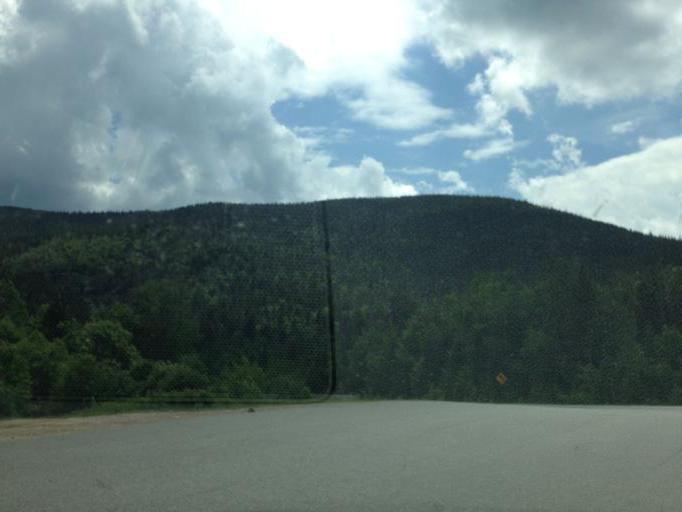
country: US
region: New Hampshire
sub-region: Grafton County
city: Woodstock
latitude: 44.0233
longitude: -71.4923
